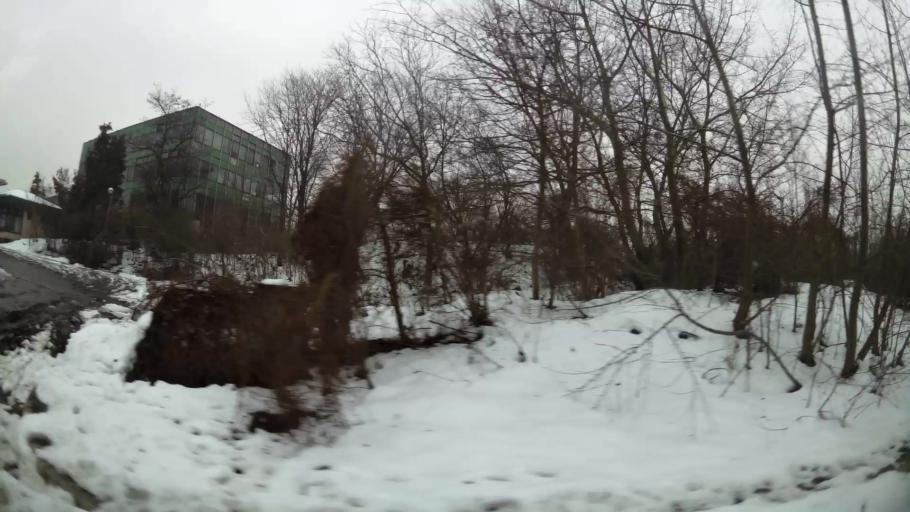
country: RS
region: Central Serbia
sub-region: Belgrade
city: Zvezdara
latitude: 44.7763
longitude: 20.5095
